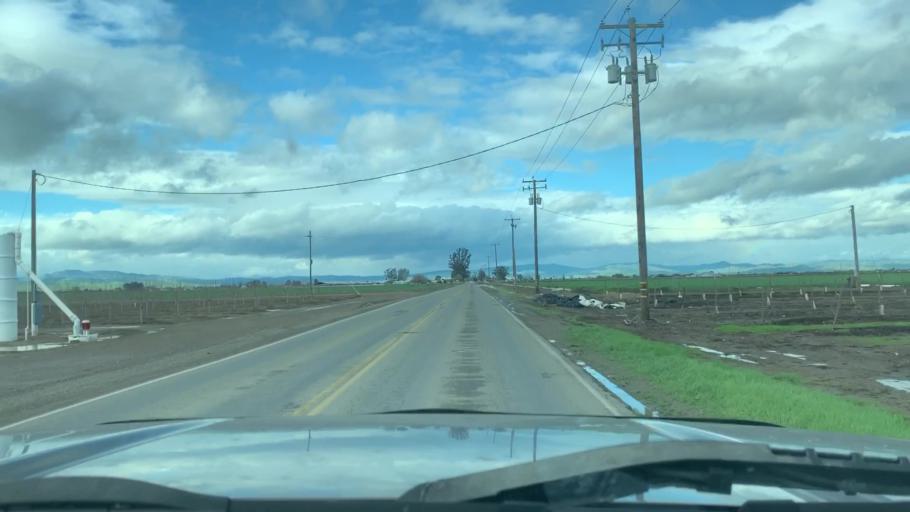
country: US
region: California
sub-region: Merced County
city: Los Banos
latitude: 37.0998
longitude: -120.8439
